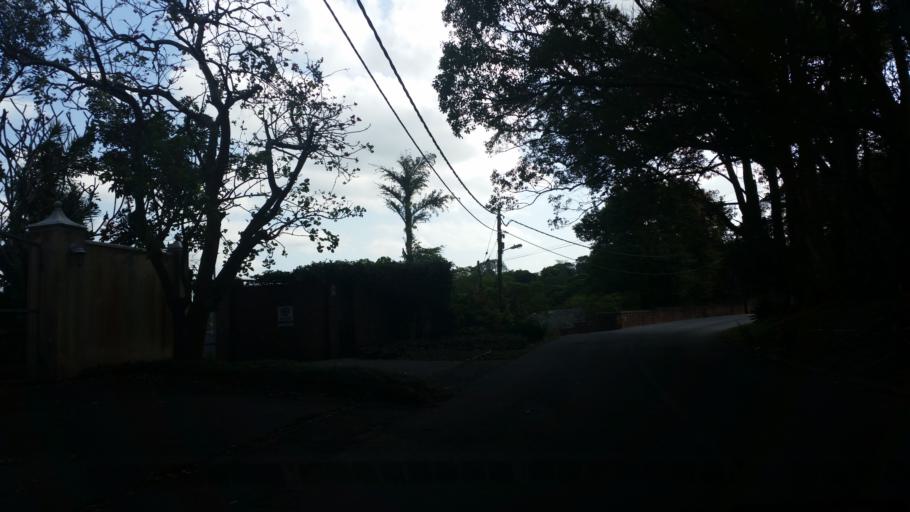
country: ZA
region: KwaZulu-Natal
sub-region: eThekwini Metropolitan Municipality
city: Berea
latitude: -29.8374
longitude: 30.9002
